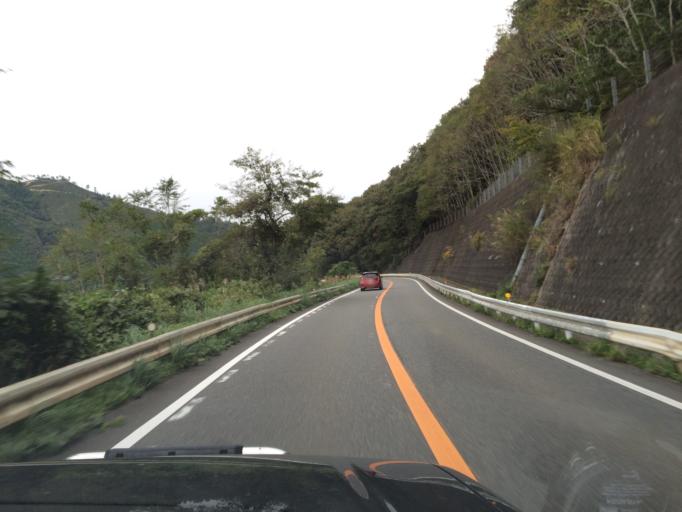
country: JP
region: Hyogo
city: Toyooka
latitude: 35.3705
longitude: 134.8174
